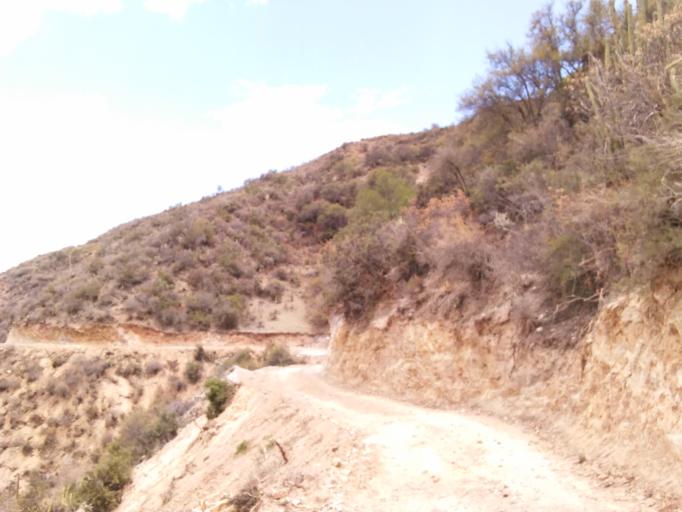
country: PE
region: Ayacucho
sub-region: Provincia de Victor Fajardo
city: Canaria
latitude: -13.8825
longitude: -73.9392
